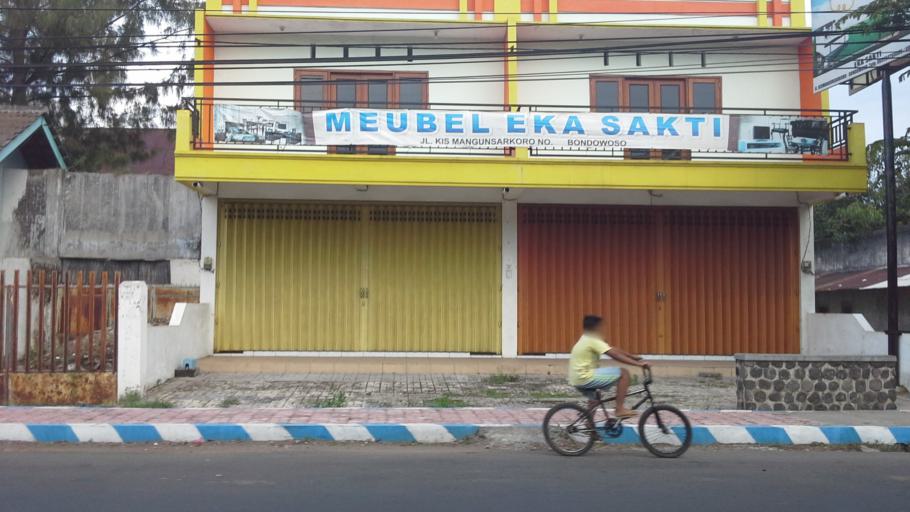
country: ID
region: East Java
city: Bondowoso
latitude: -7.9267
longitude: 113.8258
